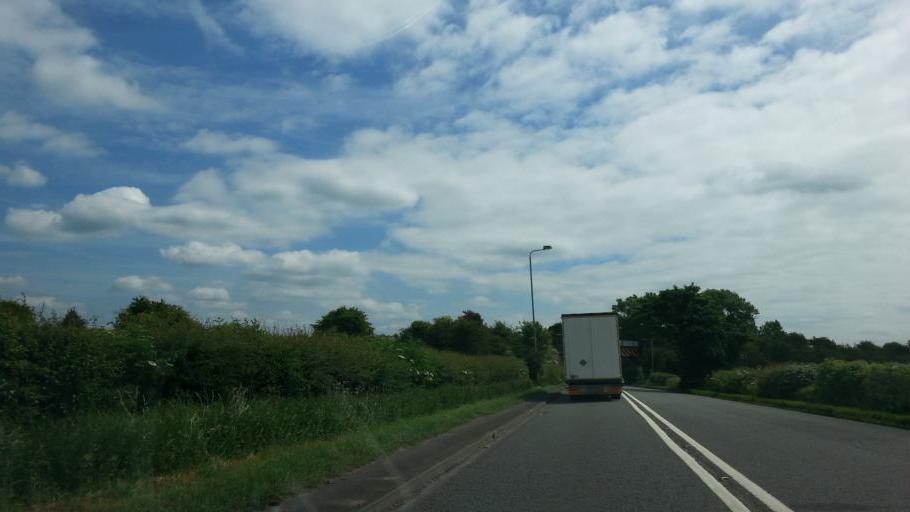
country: GB
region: England
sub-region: Nottinghamshire
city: West Bridgford
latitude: 52.9011
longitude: -1.1113
